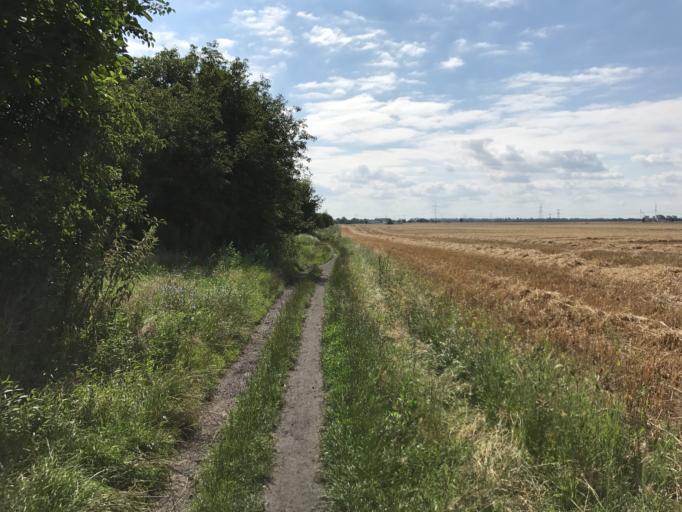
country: DE
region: Berlin
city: Karow
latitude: 52.6104
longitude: 13.4990
